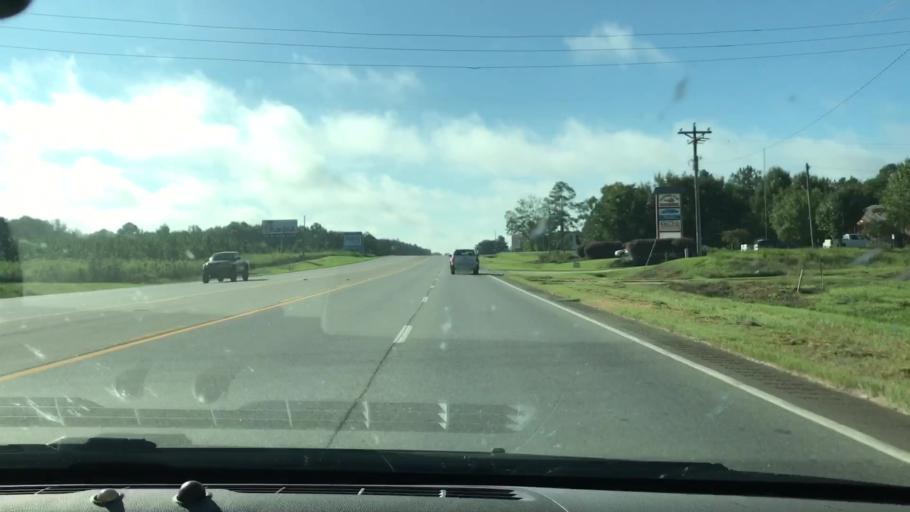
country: US
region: Georgia
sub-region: Terrell County
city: Dawson
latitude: 31.7549
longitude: -84.4256
